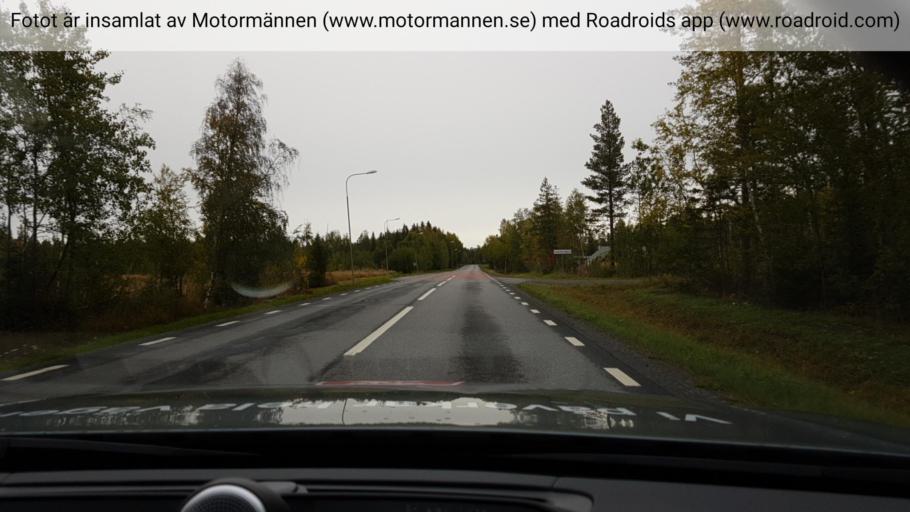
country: SE
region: Jaemtland
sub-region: Stroemsunds Kommun
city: Stroemsund
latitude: 63.8343
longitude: 15.5173
